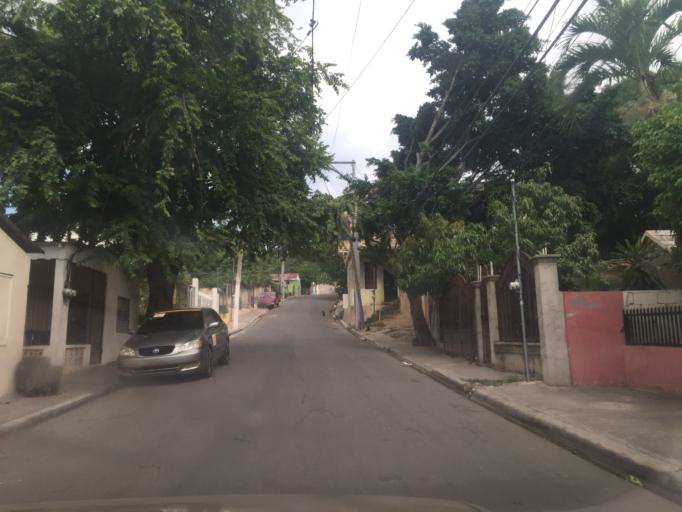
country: DO
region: Santiago
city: Santiago de los Caballeros
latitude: 19.4233
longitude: -70.7142
